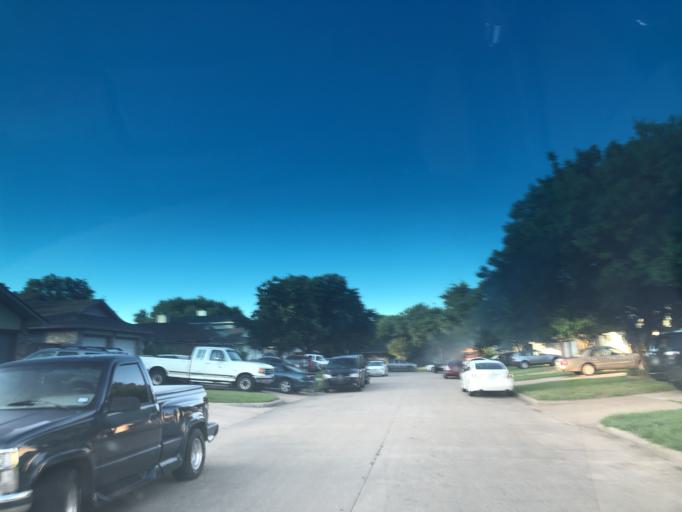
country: US
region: Texas
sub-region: Dallas County
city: Grand Prairie
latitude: 32.6941
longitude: -97.0177
